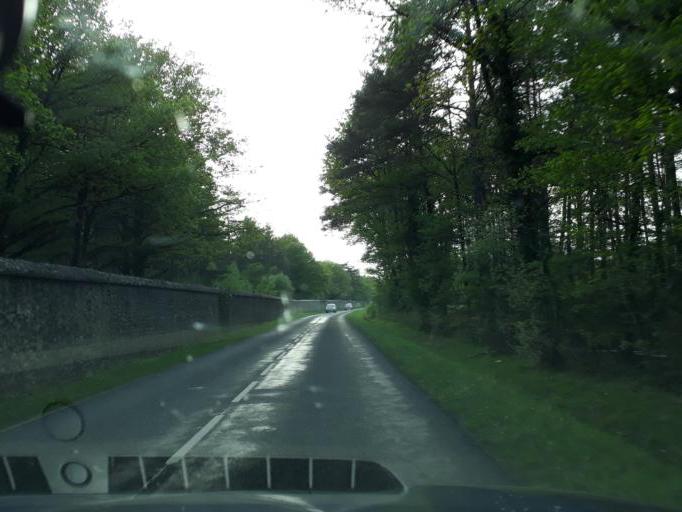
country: FR
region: Centre
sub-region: Departement du Loir-et-Cher
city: Muides-sur-Loire
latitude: 47.6507
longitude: 1.5738
